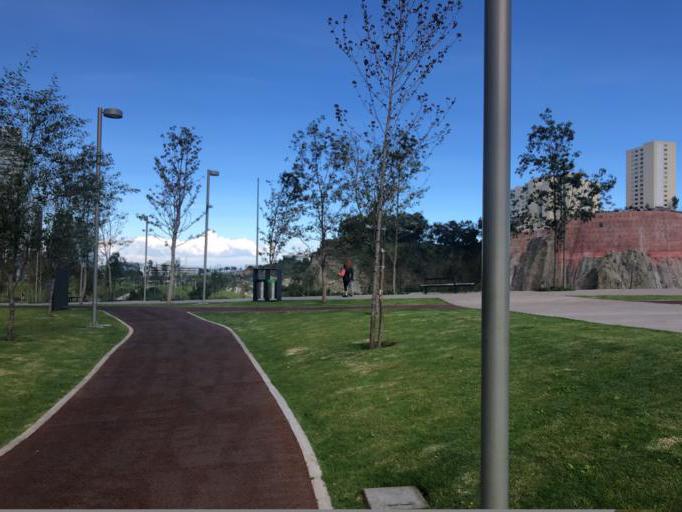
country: MX
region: Mexico City
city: Cuajimalpa
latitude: 19.3554
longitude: -99.2745
